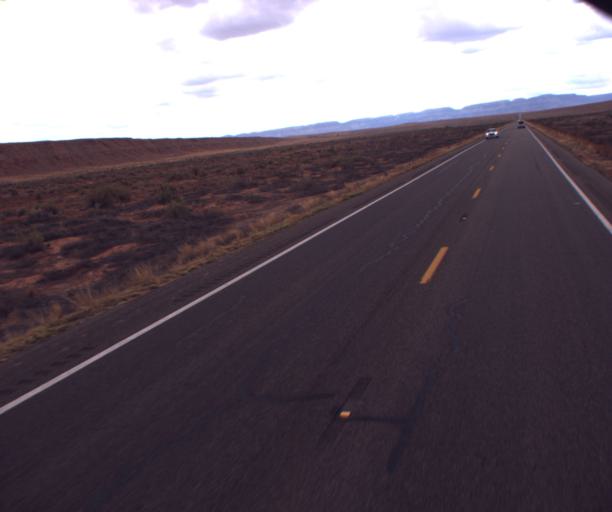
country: US
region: Arizona
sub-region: Navajo County
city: Kayenta
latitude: 36.7617
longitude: -110.0419
